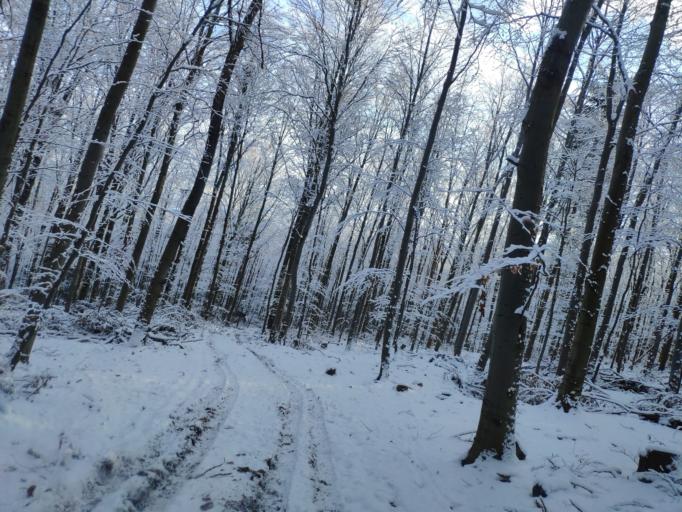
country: SK
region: Kosicky
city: Moldava nad Bodvou
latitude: 48.7483
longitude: 21.0833
